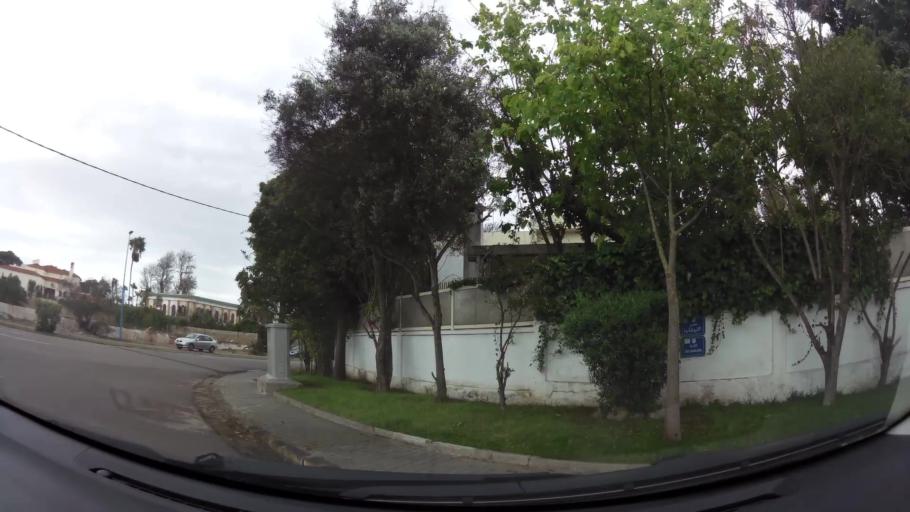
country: MA
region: Grand Casablanca
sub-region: Casablanca
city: Casablanca
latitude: 33.5828
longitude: -7.6664
